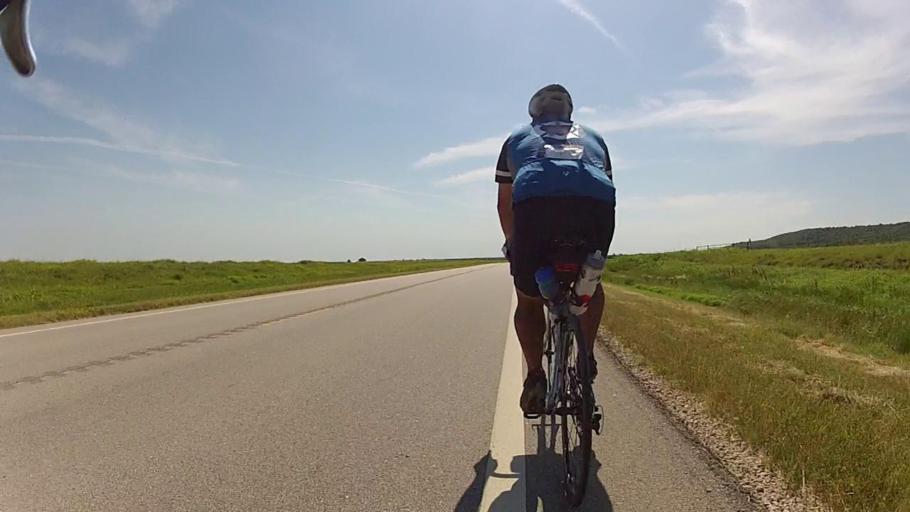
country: US
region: Kansas
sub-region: Chautauqua County
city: Sedan
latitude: 37.1065
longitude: -96.5509
